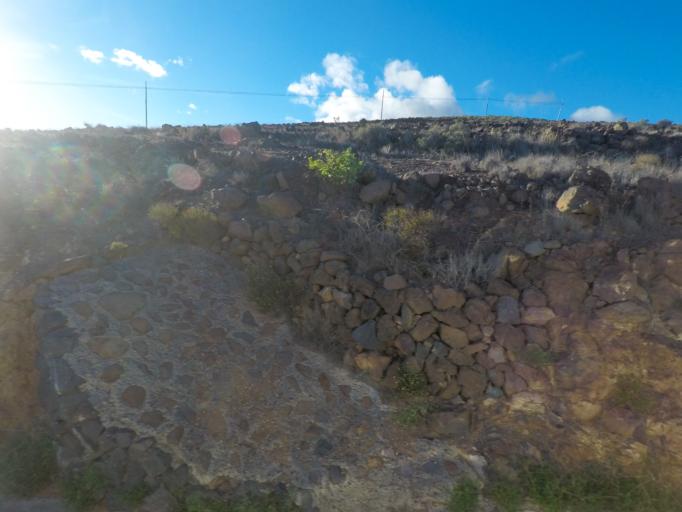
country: ES
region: Canary Islands
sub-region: Provincia de Santa Cruz de Tenerife
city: Alajero
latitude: 28.0533
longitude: -17.1998
